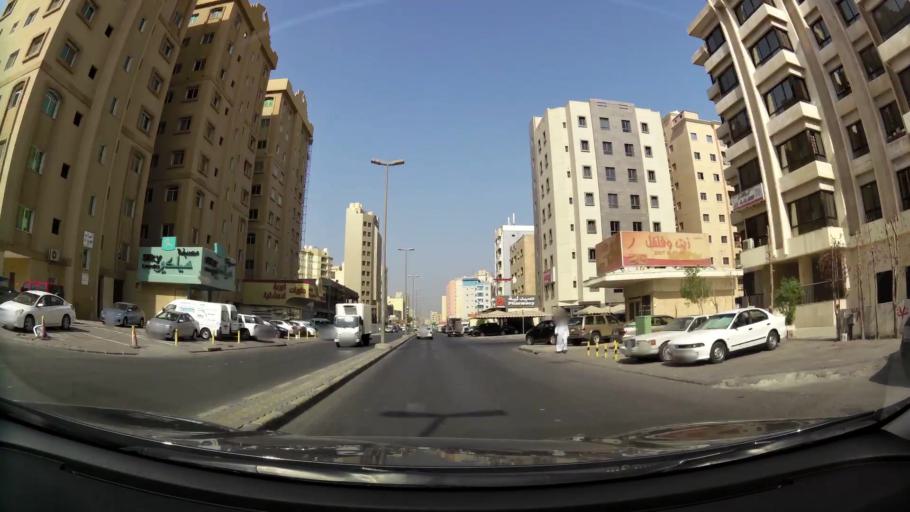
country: KW
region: Muhafazat Hawalli
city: Hawalli
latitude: 29.3352
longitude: 48.0319
